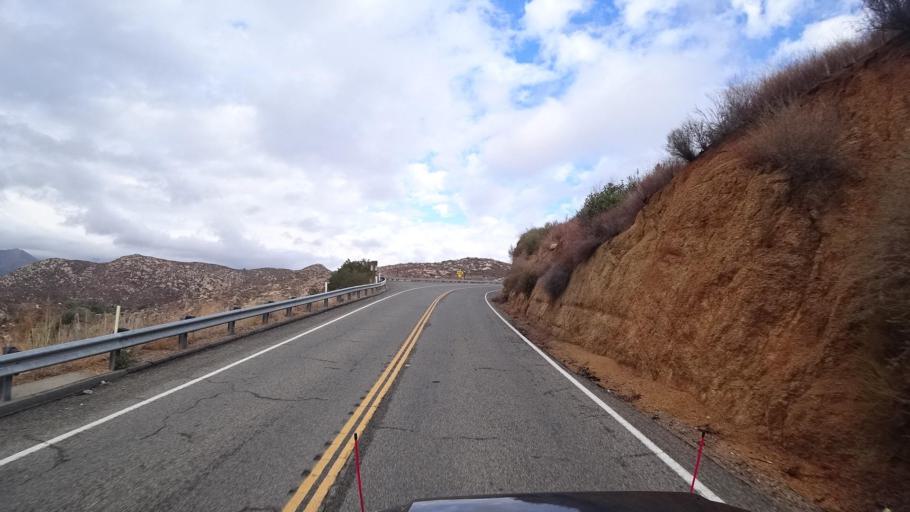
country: MX
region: Baja California
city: Tecate
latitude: 32.6029
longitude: -116.6335
